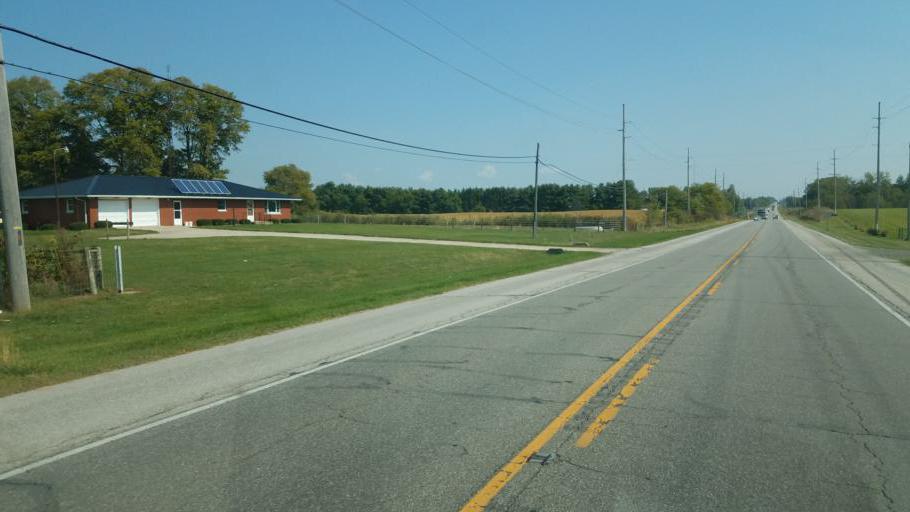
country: US
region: Indiana
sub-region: LaGrange County
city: Lagrange
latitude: 41.6415
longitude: -85.3984
